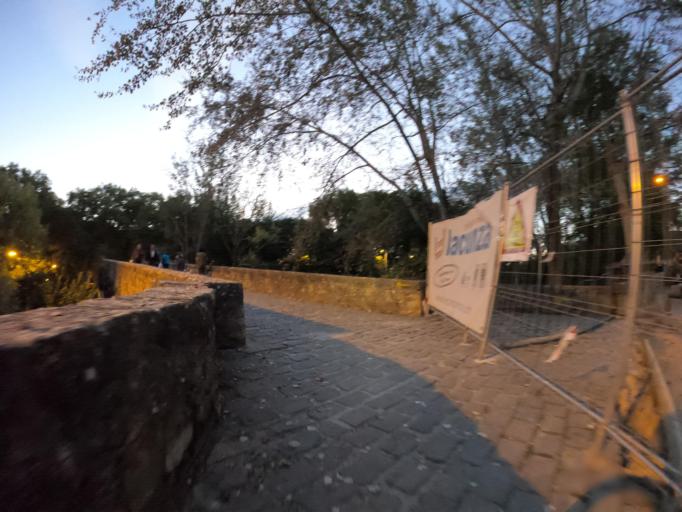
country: ES
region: Navarre
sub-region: Provincia de Navarra
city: Pamplona
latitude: 42.8211
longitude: -1.6377
